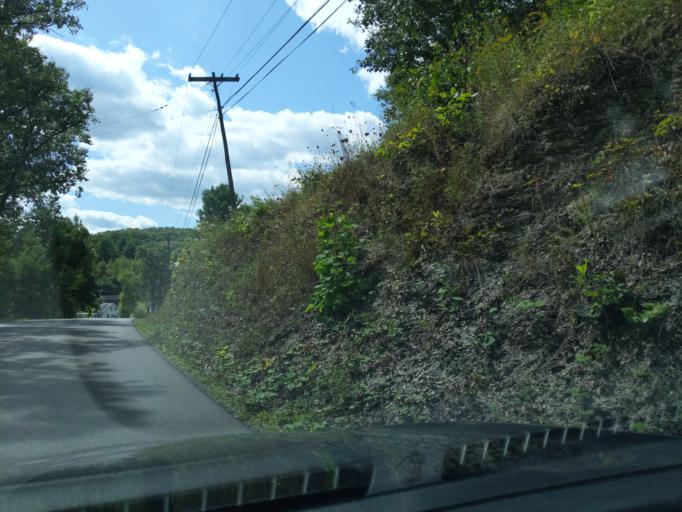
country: US
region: Pennsylvania
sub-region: Blair County
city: Tyrone
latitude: 40.7051
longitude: -78.2172
